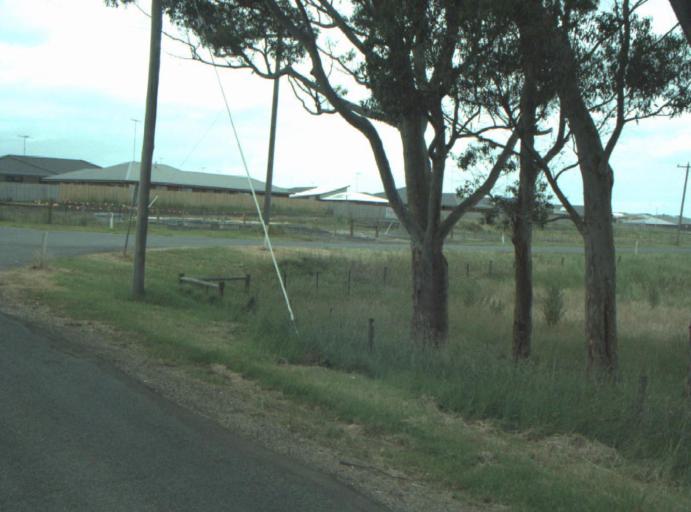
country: AU
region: Victoria
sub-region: Greater Geelong
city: Wandana Heights
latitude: -38.2176
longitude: 144.3007
